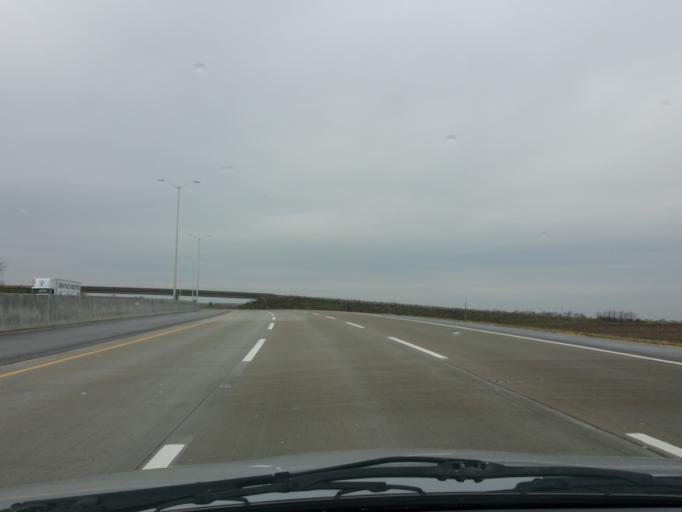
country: US
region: Illinois
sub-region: Boone County
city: Belvidere
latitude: 42.2334
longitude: -88.7847
